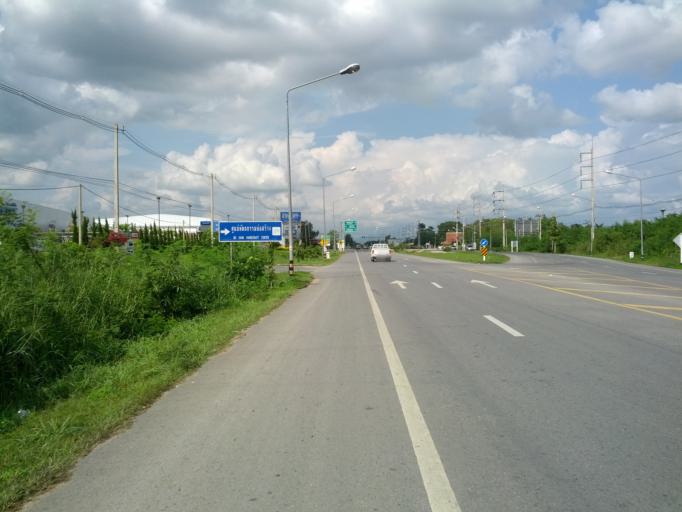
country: TH
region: Chiang Mai
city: San Kamphaeng
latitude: 18.7678
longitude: 99.0667
